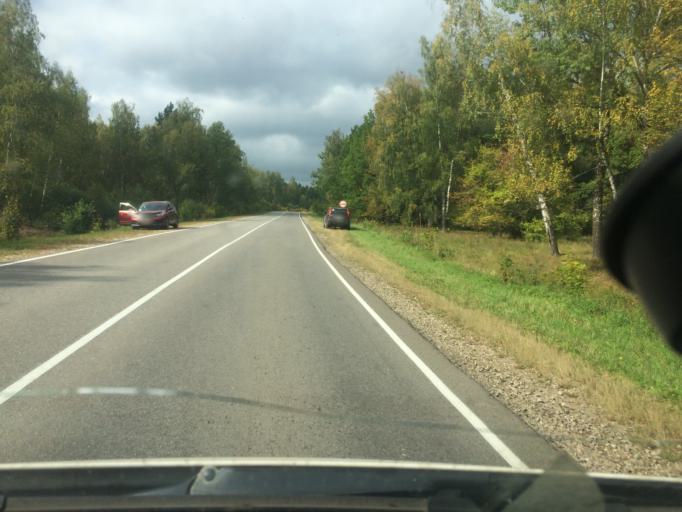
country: RU
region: Tula
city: Suvorov
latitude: 54.0544
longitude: 36.5698
